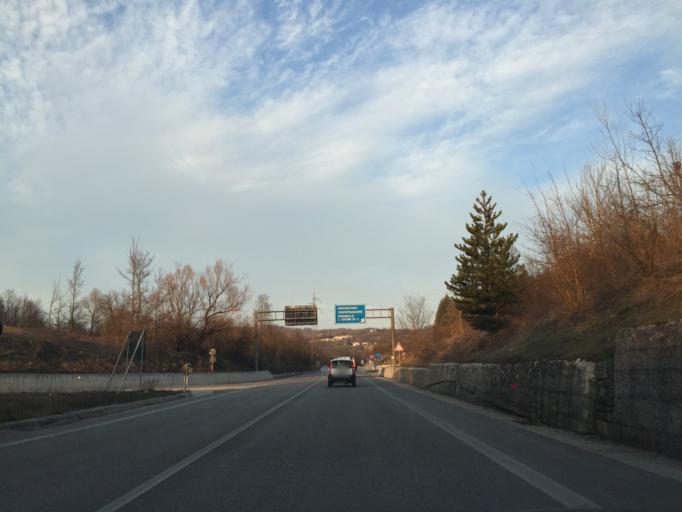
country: IT
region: Molise
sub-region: Provincia di Campobasso
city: Vinchiaturo
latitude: 41.4916
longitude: 14.6022
